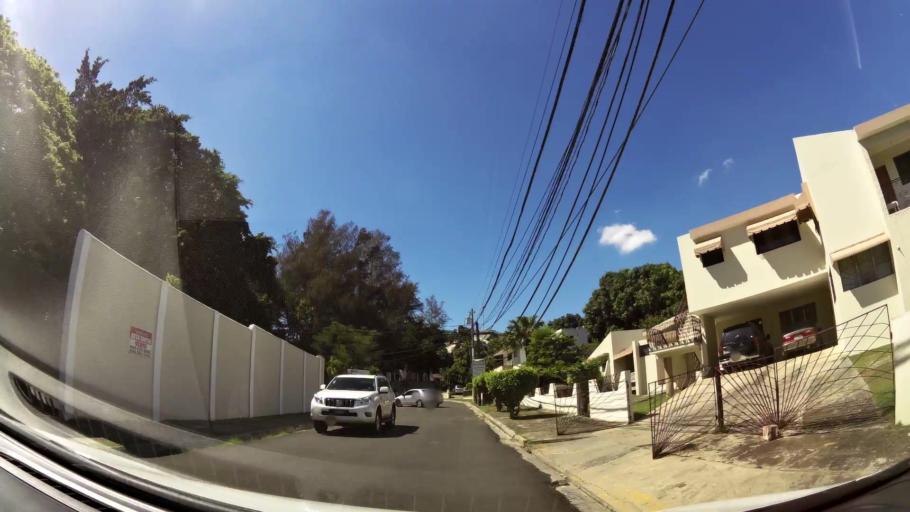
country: DO
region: Santiago
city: Santiago de los Caballeros
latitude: 19.4487
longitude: -70.6897
